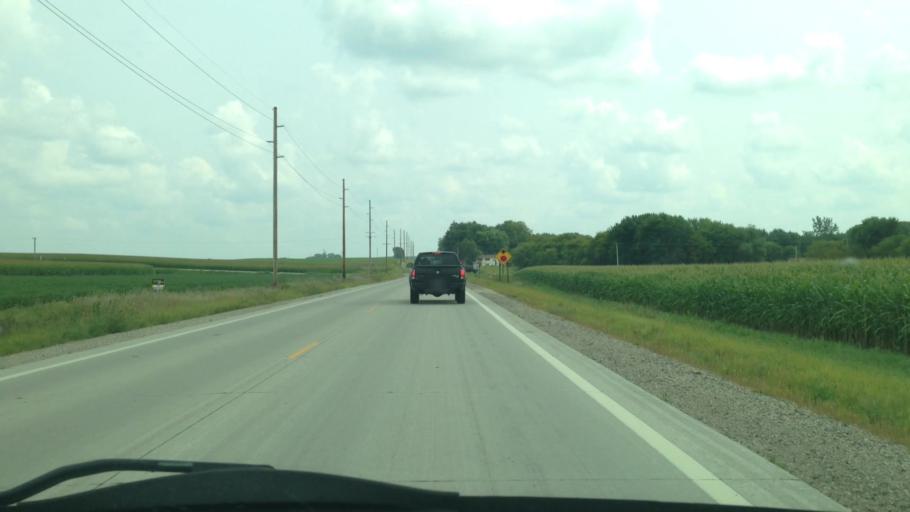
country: US
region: Minnesota
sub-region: Wabasha County
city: Elgin
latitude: 44.1364
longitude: -92.2627
